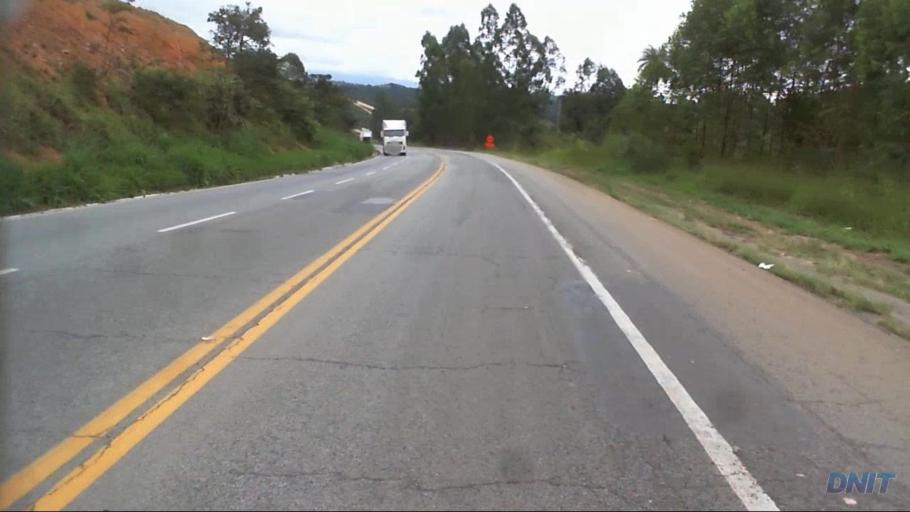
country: BR
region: Minas Gerais
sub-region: Barao De Cocais
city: Barao de Cocais
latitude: -19.7940
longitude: -43.4264
